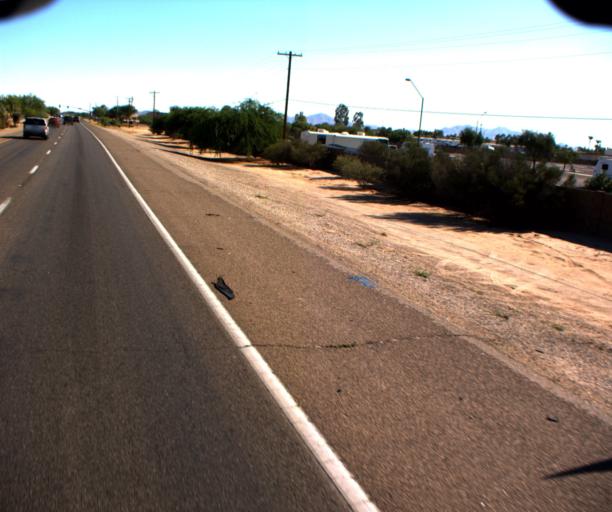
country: US
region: Arizona
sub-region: Pinal County
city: Casa Grande
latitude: 32.9202
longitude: -111.7569
